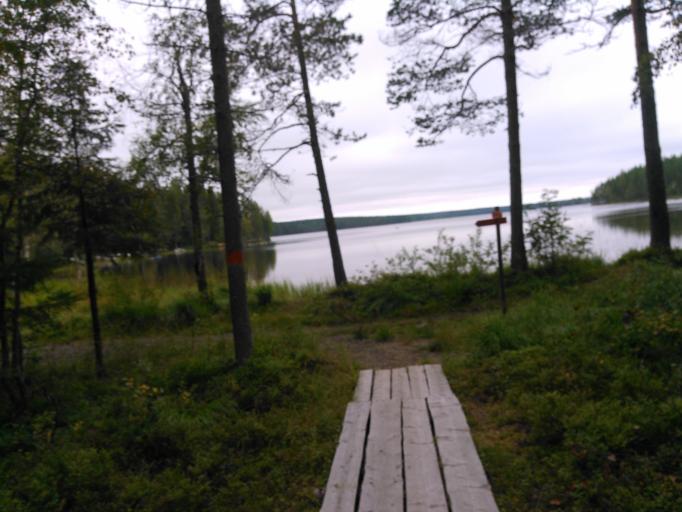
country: SE
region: Vaesterbotten
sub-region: Umea Kommun
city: Ersmark
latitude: 63.9345
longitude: 20.3865
